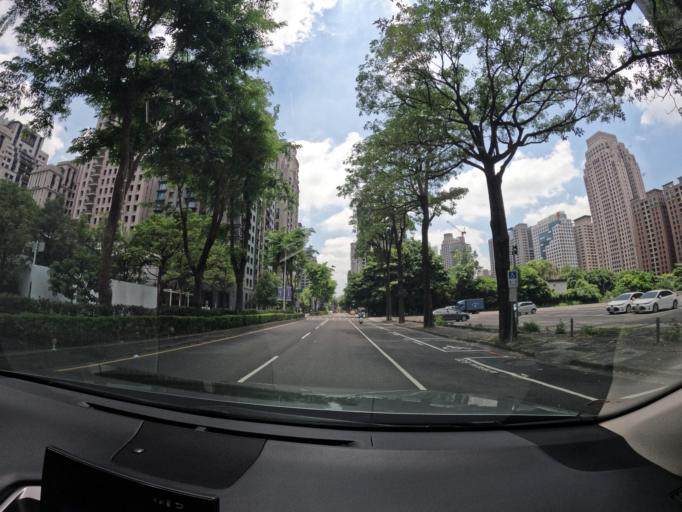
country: TW
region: Taiwan
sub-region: Taichung City
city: Taichung
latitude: 24.1599
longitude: 120.6408
